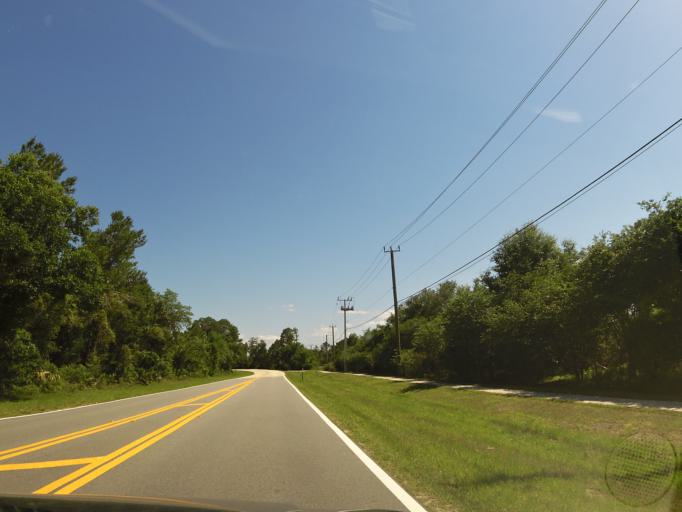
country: US
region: Florida
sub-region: Flagler County
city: Flagler Beach
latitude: 29.4091
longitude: -81.1481
